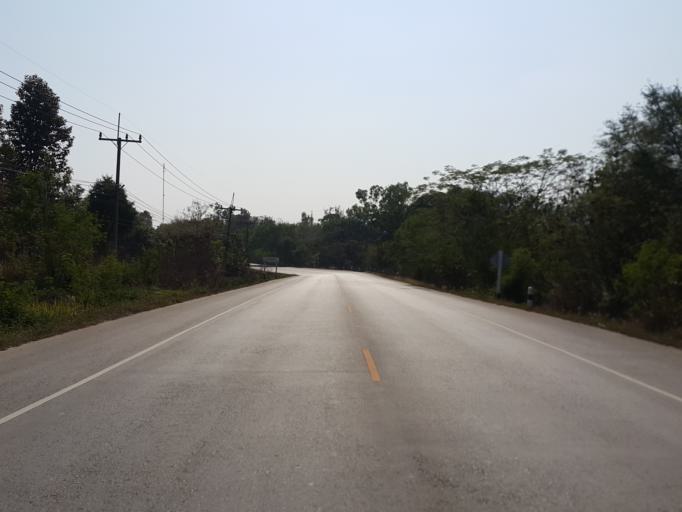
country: TH
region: Lampang
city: Chae Hom
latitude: 18.7628
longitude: 99.5723
